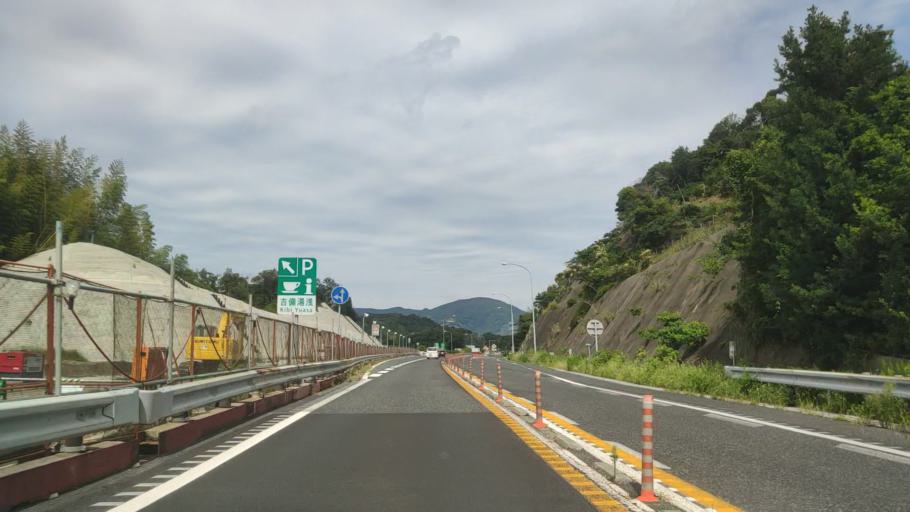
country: JP
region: Wakayama
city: Kainan
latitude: 34.0344
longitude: 135.2009
